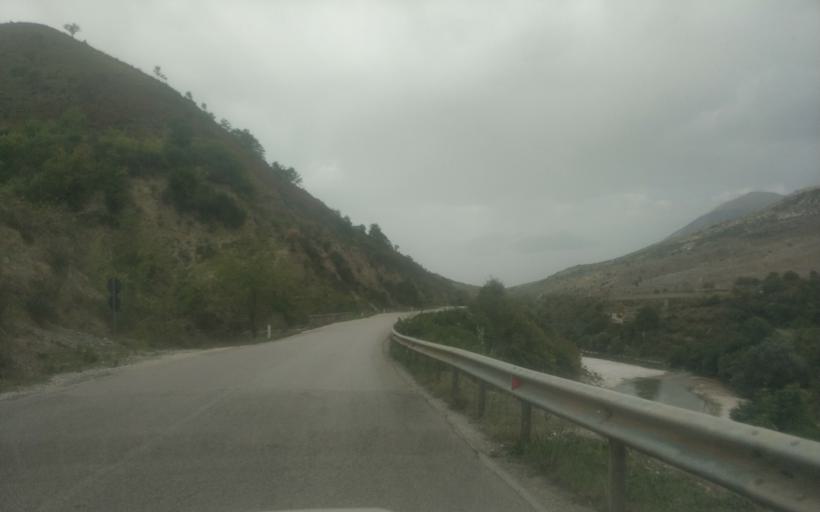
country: AL
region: Gjirokaster
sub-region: Rrethi i Gjirokastres
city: Picar
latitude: 40.2301
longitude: 20.0837
